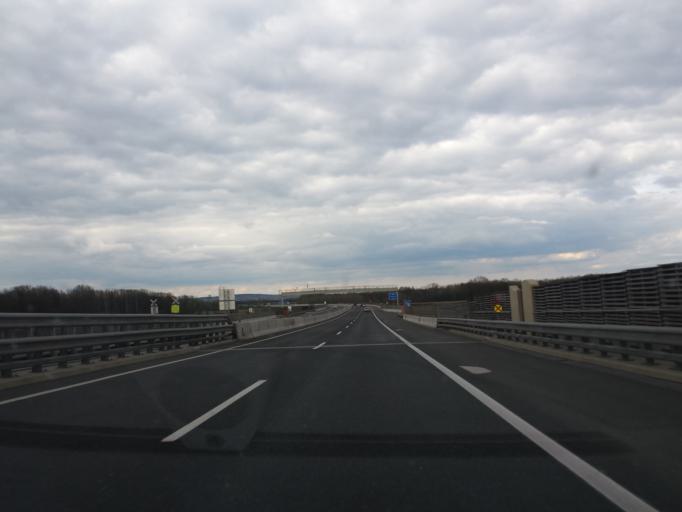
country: AT
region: Lower Austria
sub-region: Politischer Bezirk Krems
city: Grafenegg
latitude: 48.3891
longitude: 15.7268
